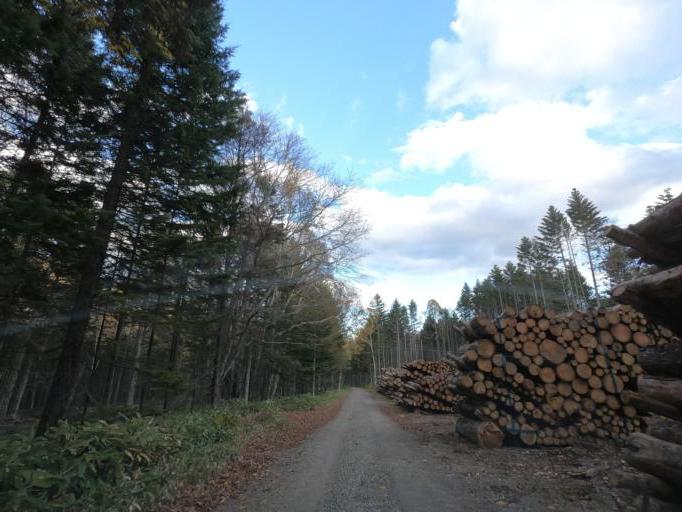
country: JP
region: Hokkaido
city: Otofuke
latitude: 43.4332
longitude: 143.1526
